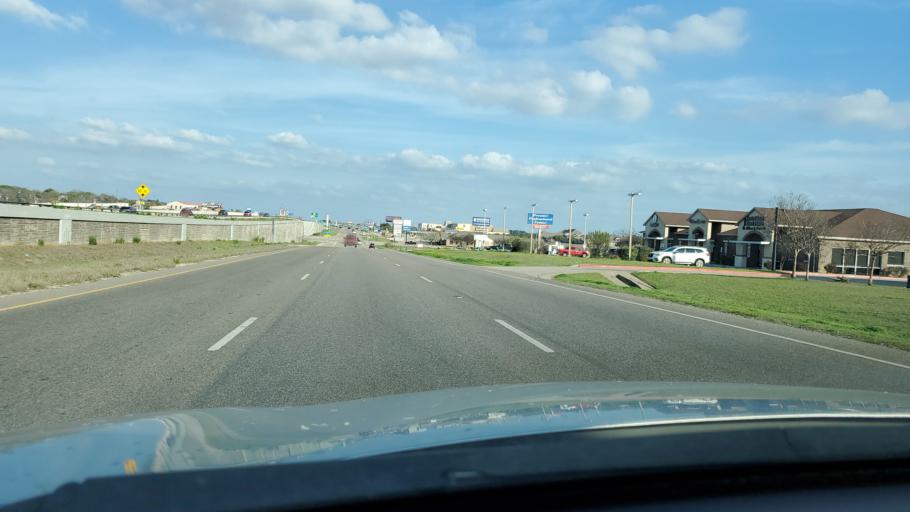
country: US
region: Texas
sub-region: Bell County
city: Harker Heights
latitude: 31.0768
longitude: -97.6916
